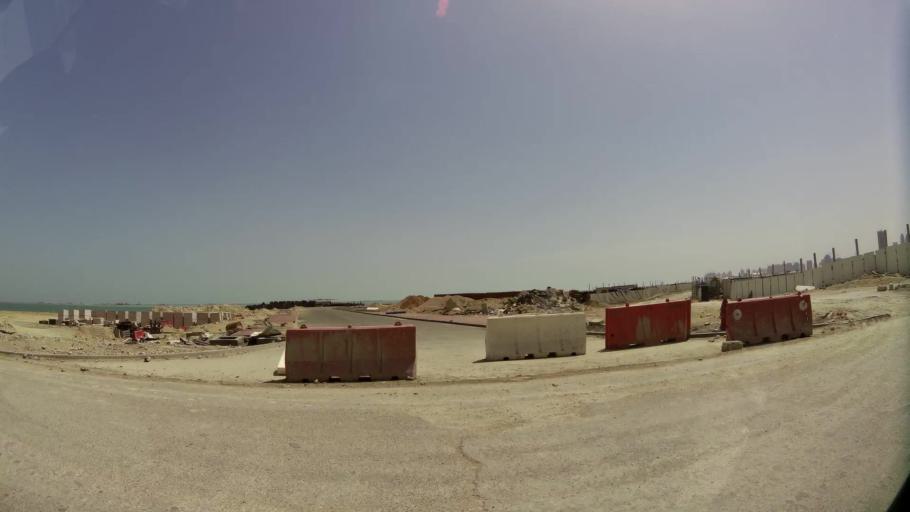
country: QA
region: Baladiyat Umm Salal
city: Umm Salal Muhammad
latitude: 25.4033
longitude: 51.5237
